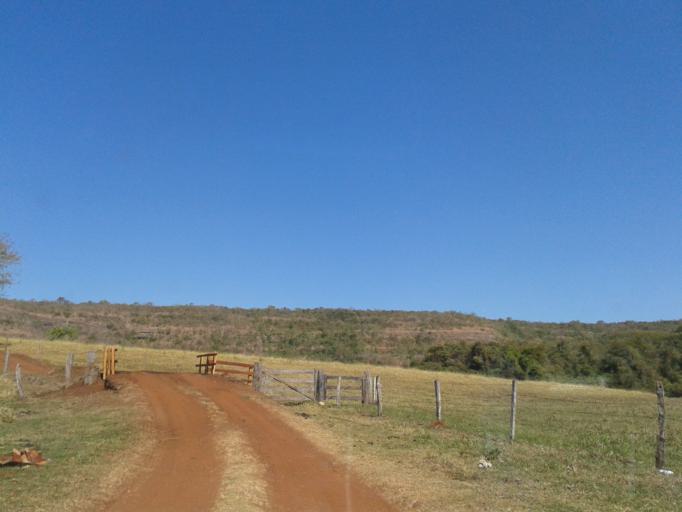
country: BR
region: Minas Gerais
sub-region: Santa Vitoria
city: Santa Vitoria
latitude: -19.1026
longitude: -49.9803
